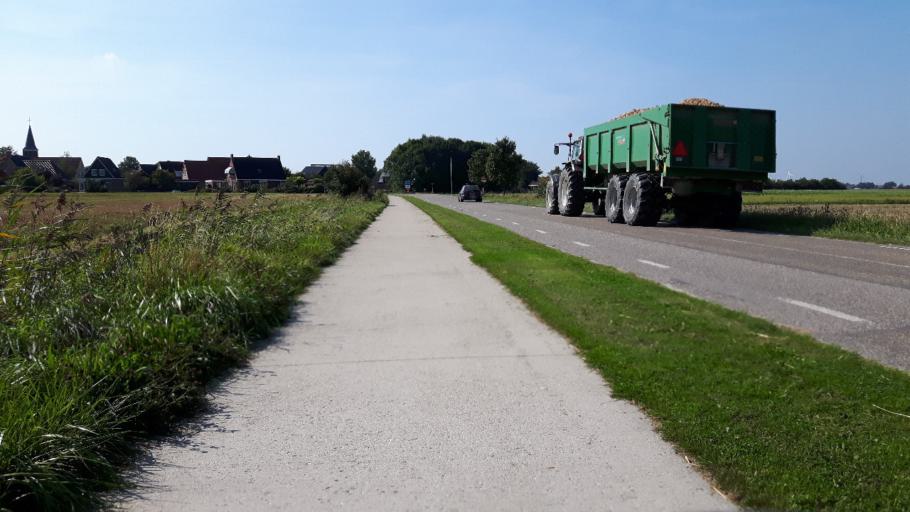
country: NL
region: Friesland
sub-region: Gemeente Franekeradeel
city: Franeker
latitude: 53.2091
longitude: 5.5492
